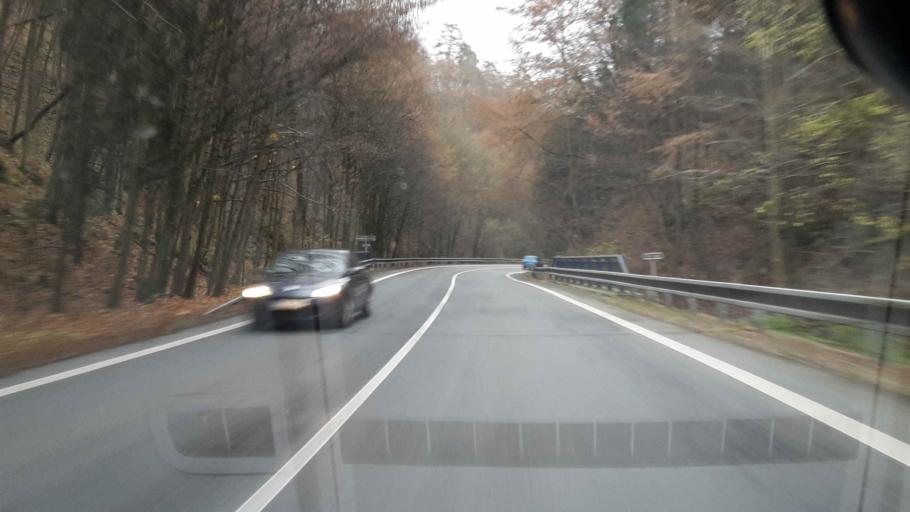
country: CZ
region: South Moravian
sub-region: Okres Blansko
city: Adamov
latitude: 49.3280
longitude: 16.6195
